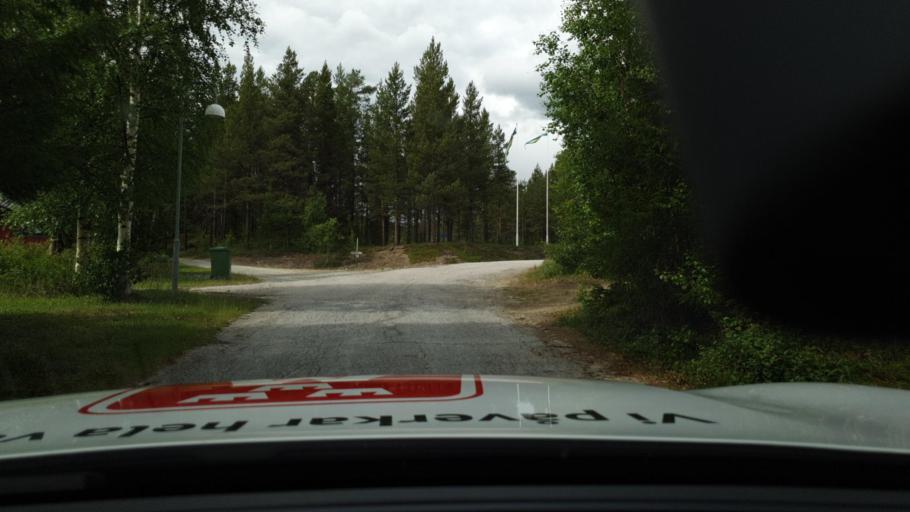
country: SE
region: Norrbotten
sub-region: Arjeplogs Kommun
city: Arjeplog
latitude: 66.8858
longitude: 18.0227
